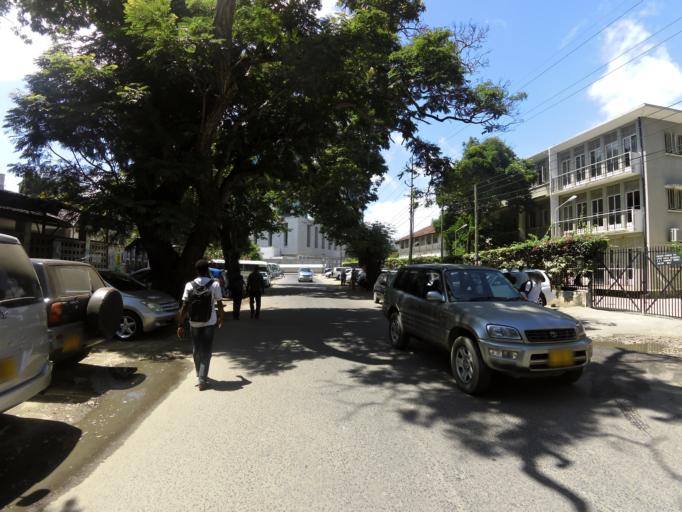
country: TZ
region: Dar es Salaam
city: Dar es Salaam
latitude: -6.8144
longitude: 39.2929
